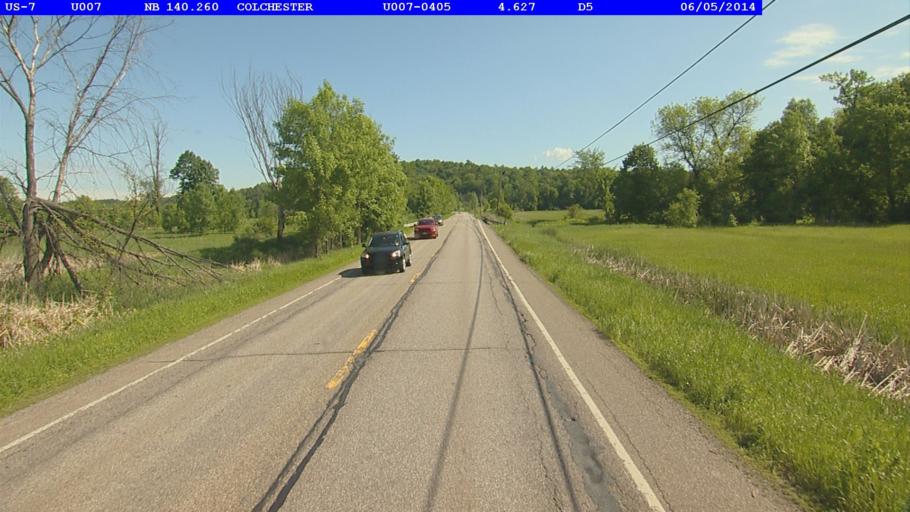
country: US
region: Vermont
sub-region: Chittenden County
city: Colchester
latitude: 44.5648
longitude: -73.1580
